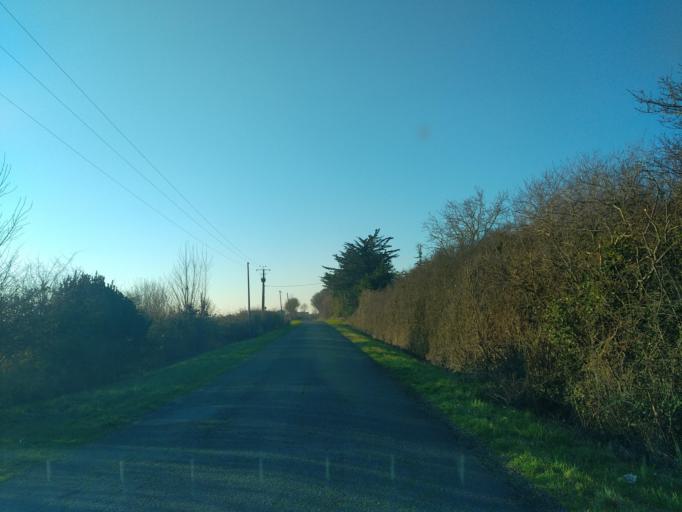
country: FR
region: Pays de la Loire
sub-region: Departement de la Vendee
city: Triaize
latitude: 46.3915
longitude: -1.2857
